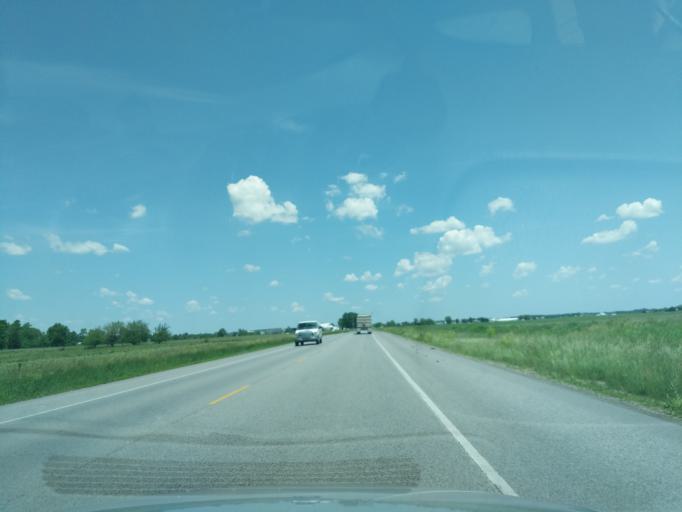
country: US
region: Indiana
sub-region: LaGrange County
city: Topeka
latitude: 41.5850
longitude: -85.5787
